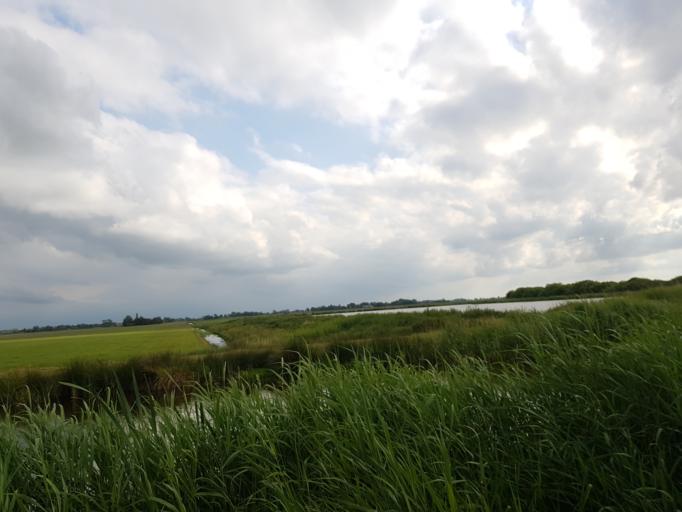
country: NL
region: Friesland
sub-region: Gemeente Smallingerland
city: Oudega
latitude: 53.0875
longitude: 5.9629
